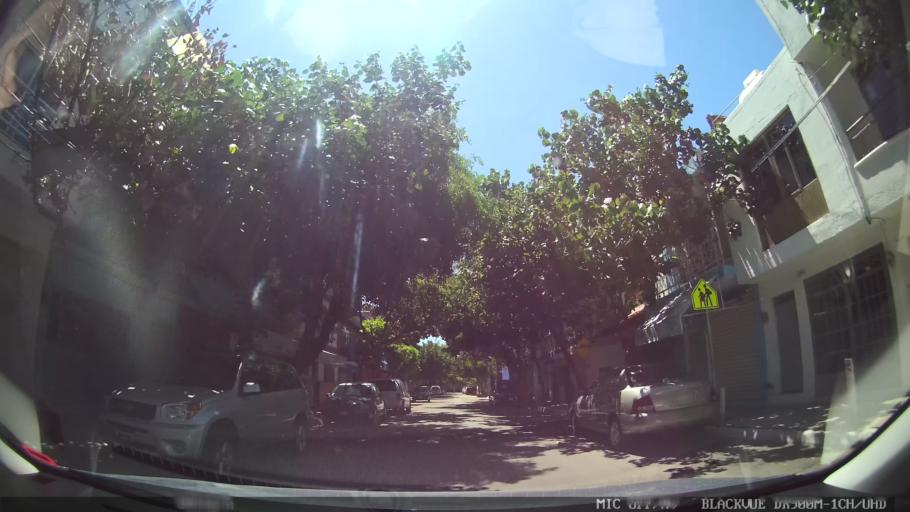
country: MX
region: Jalisco
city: Tlaquepaque
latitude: 20.6704
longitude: -103.2843
